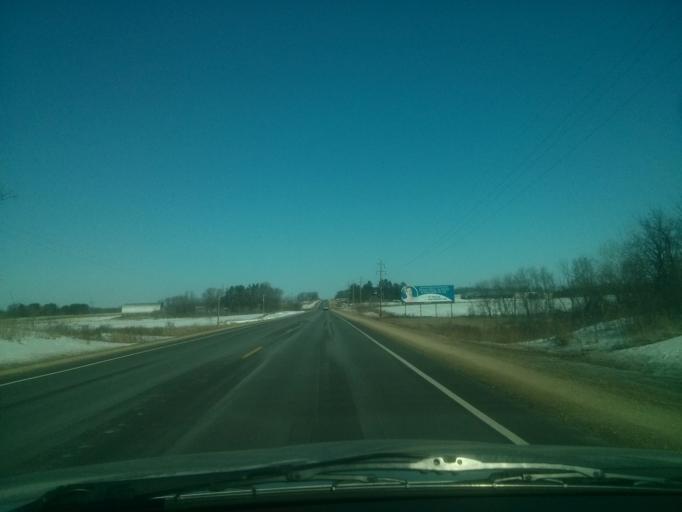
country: US
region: Wisconsin
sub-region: Polk County
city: Clear Lake
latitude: 45.1472
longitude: -92.2820
